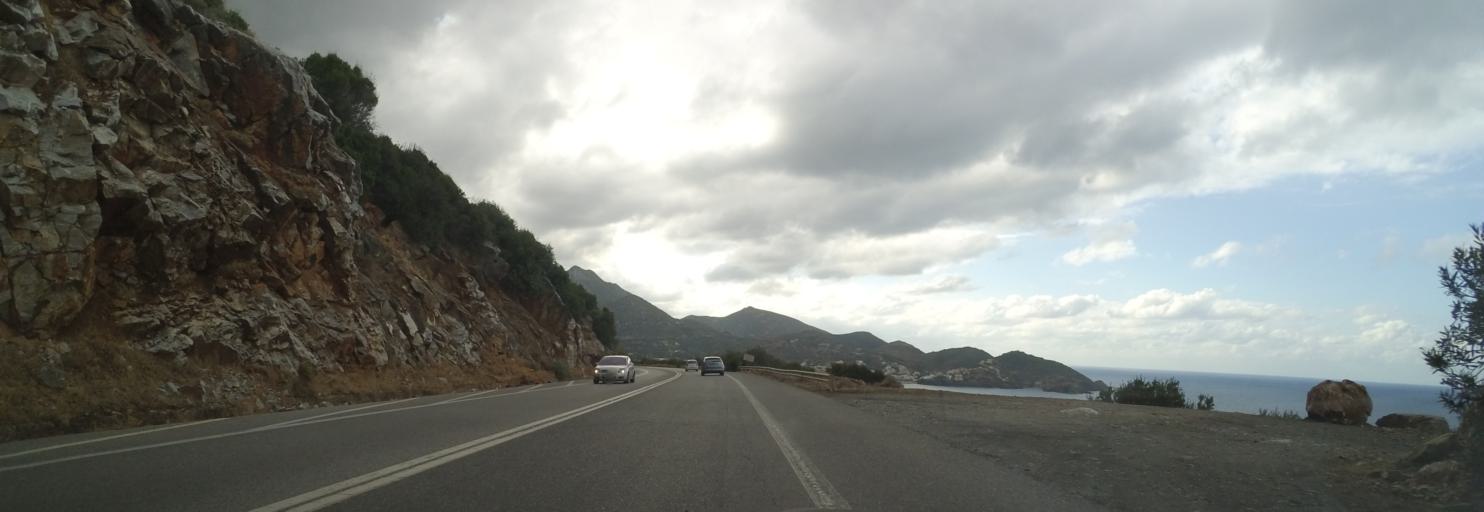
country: GR
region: Crete
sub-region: Nomos Rethymnis
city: Perama
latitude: 35.4091
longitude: 24.8029
